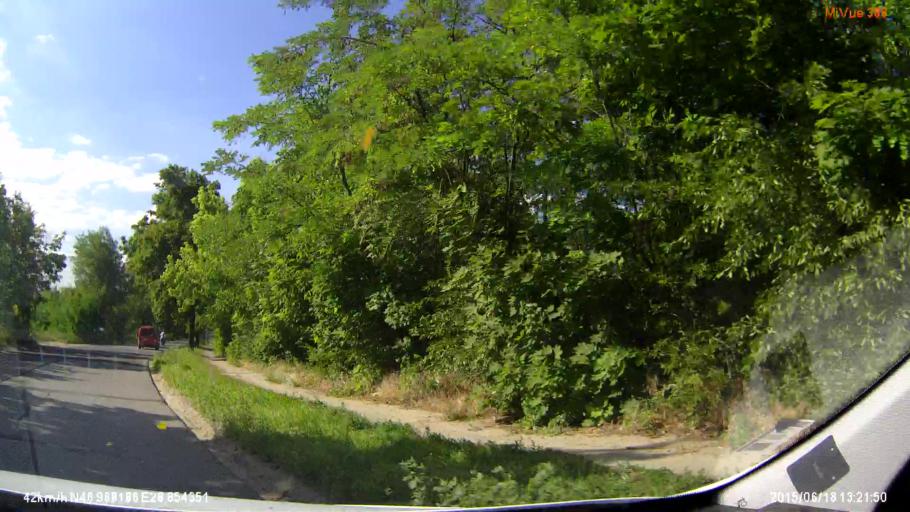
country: MD
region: Chisinau
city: Chisinau
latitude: 46.9681
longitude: 28.8544
